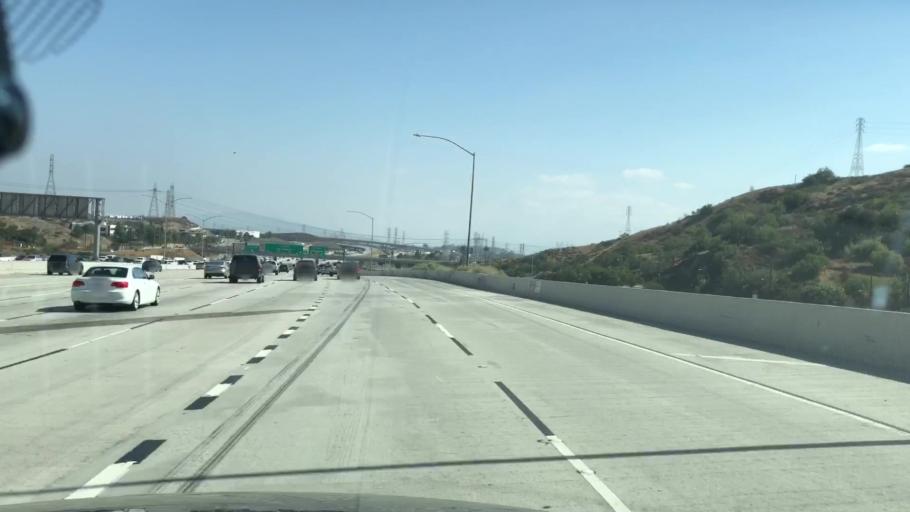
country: US
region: California
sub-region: Los Angeles County
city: San Fernando
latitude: 34.3241
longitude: -118.5023
